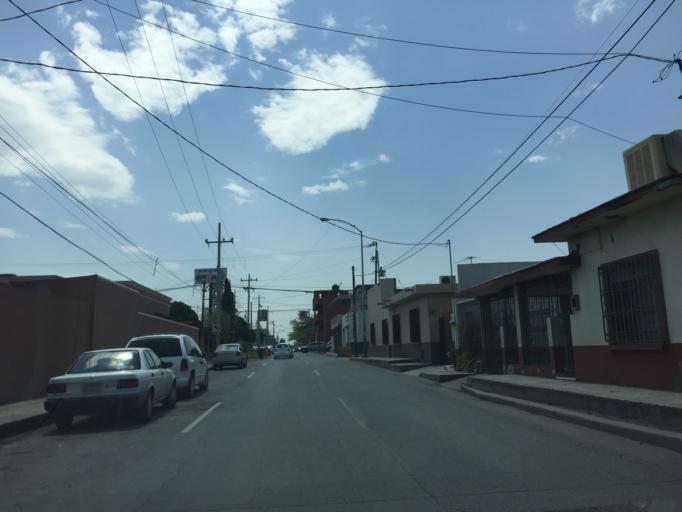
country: MX
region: Nuevo Leon
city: Apodaca
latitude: 25.7835
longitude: -100.1893
